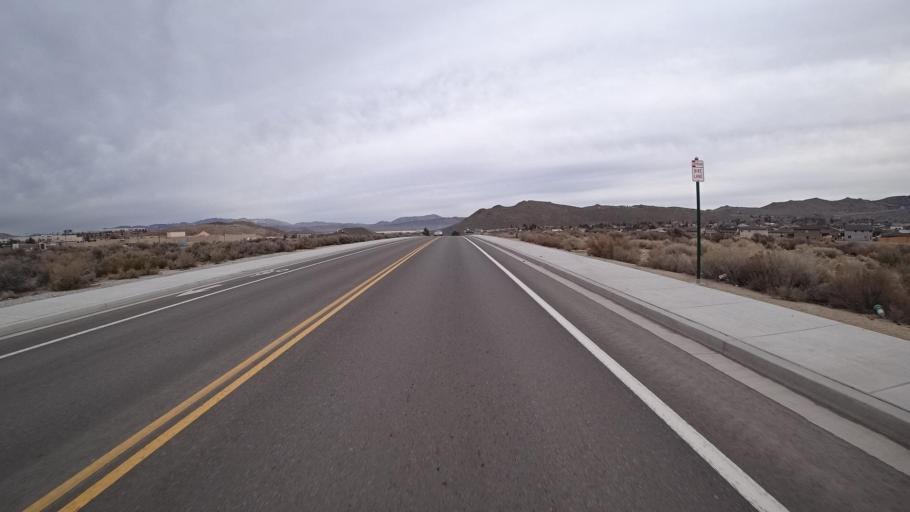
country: US
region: Nevada
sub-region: Washoe County
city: Golden Valley
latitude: 39.6098
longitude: -119.8449
